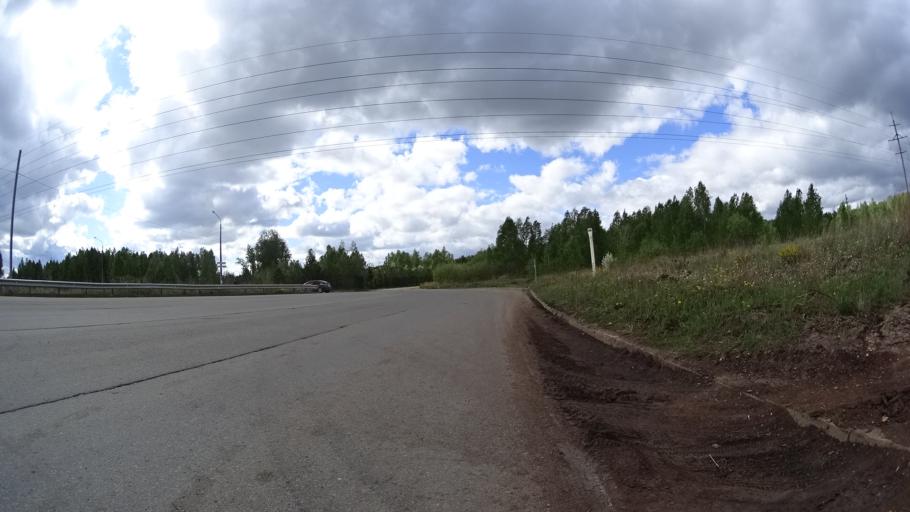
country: RU
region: Chelyabinsk
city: Sargazy
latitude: 55.1535
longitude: 61.2662
